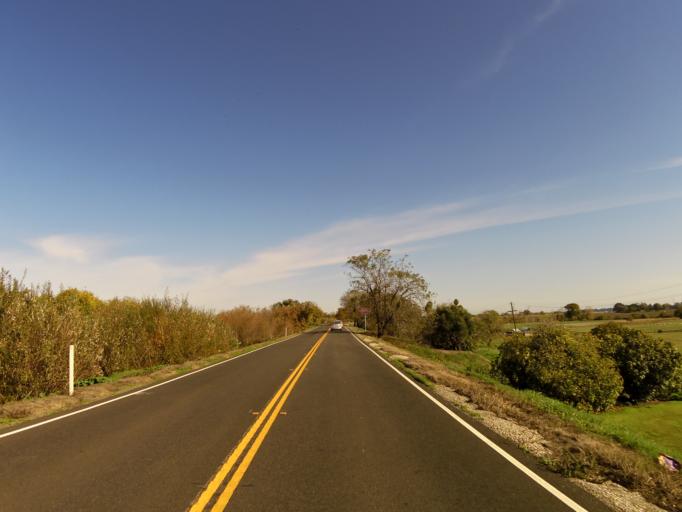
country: US
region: California
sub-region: Solano County
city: Rio Vista
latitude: 38.1725
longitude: -121.6659
